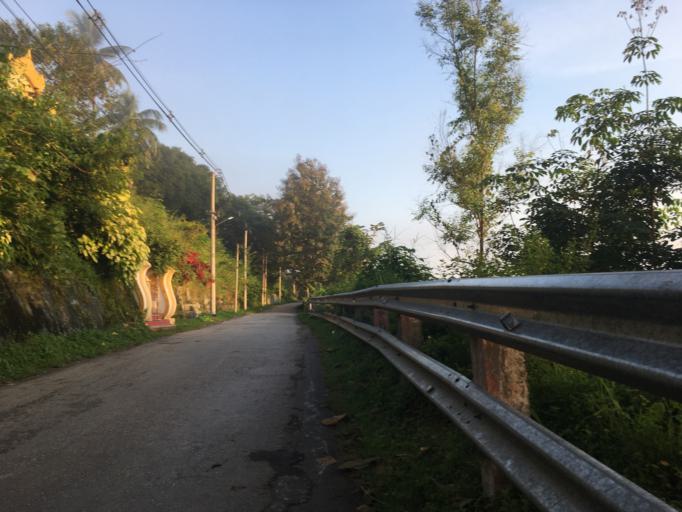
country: MM
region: Mon
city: Mawlamyine
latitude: 16.4729
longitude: 97.6303
